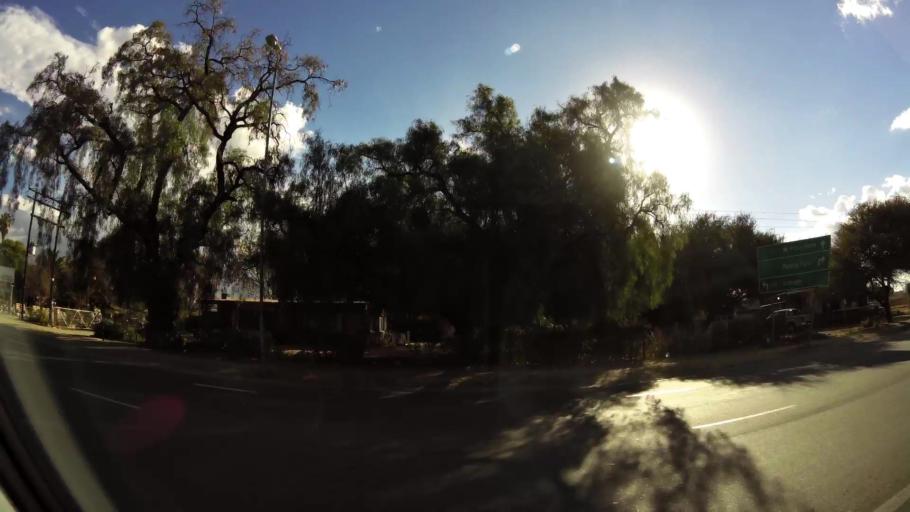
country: ZA
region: Limpopo
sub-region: Capricorn District Municipality
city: Polokwane
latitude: -23.9288
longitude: 29.4508
